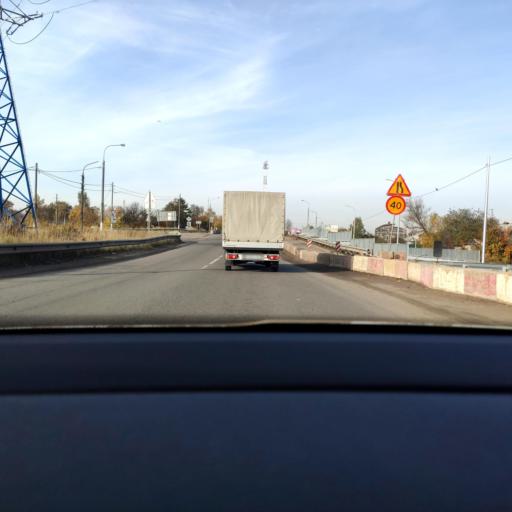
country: RU
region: Moskovskaya
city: Lesnyye Polyany
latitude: 55.9863
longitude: 37.8746
